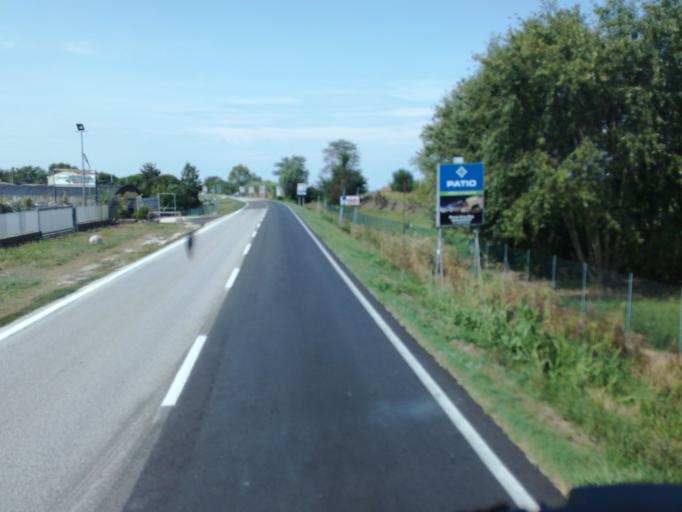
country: IT
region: Veneto
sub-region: Provincia di Rovigo
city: Loreo
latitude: 45.0597
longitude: 12.1825
